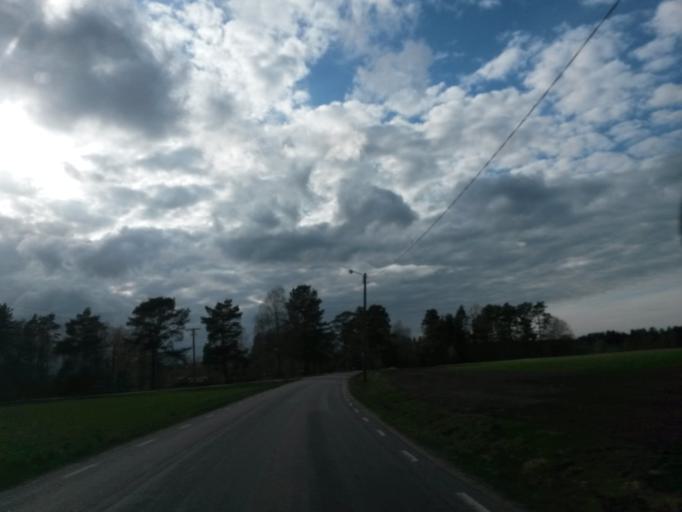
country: SE
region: Vaestra Goetaland
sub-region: Vargarda Kommun
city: Jonstorp
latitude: 58.0136
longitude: 12.6534
